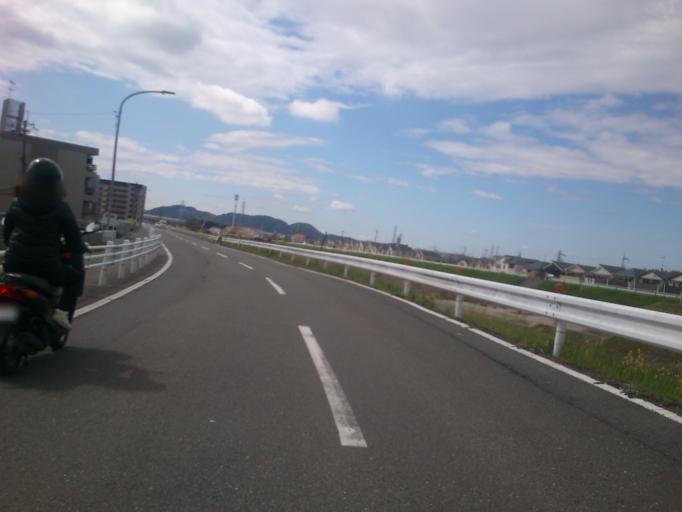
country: JP
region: Kyoto
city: Yawata
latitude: 34.9150
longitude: 135.7020
